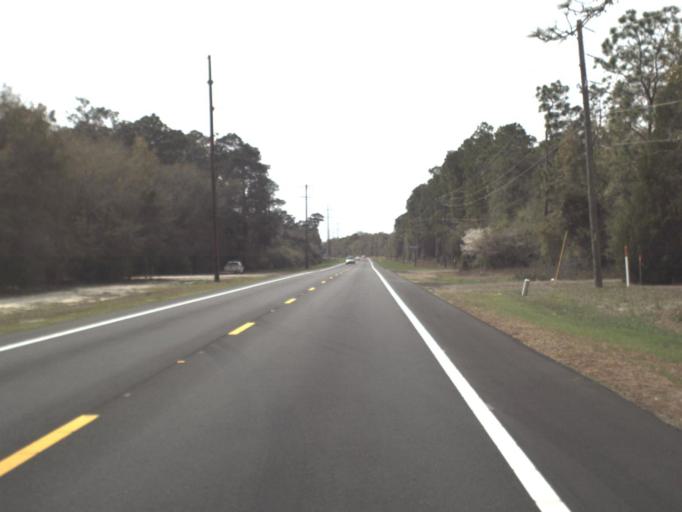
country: US
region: Florida
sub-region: Gadsden County
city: Midway
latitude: 30.4406
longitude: -84.4565
